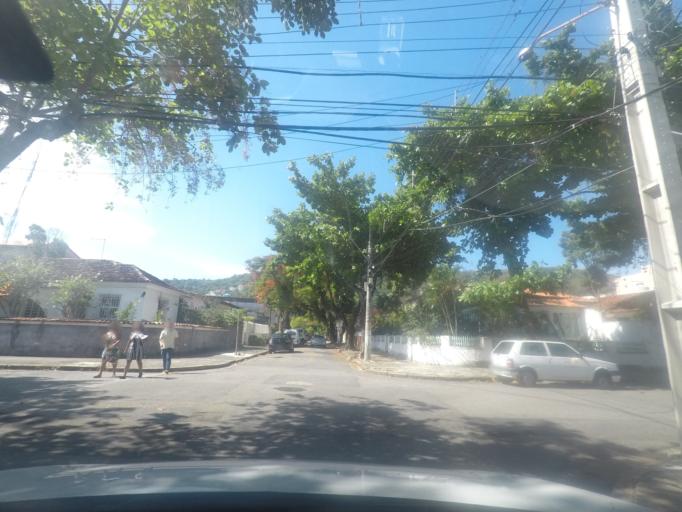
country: BR
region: Rio de Janeiro
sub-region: Niteroi
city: Niteroi
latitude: -22.9189
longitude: -43.0914
